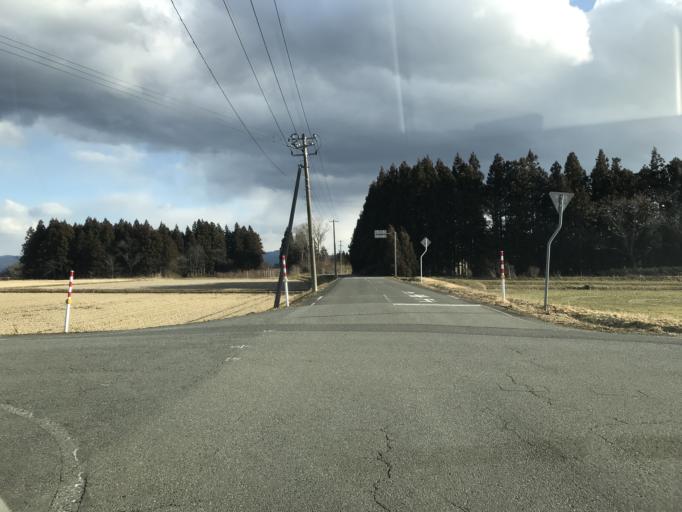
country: JP
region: Iwate
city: Mizusawa
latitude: 39.0992
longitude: 141.0290
